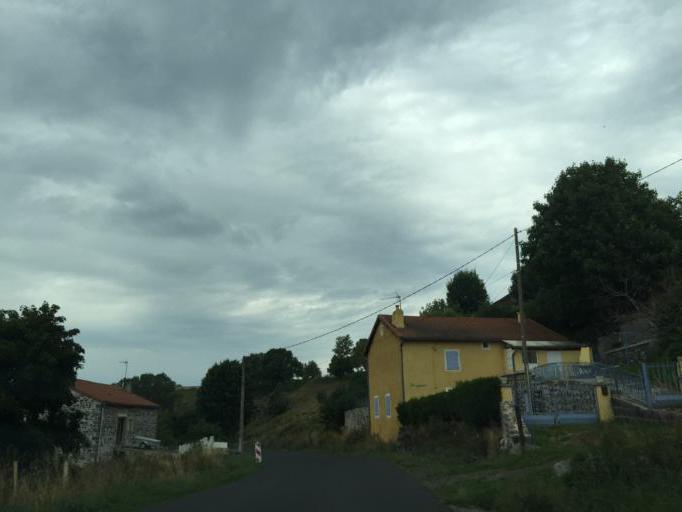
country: FR
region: Languedoc-Roussillon
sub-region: Departement de la Lozere
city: Langogne
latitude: 44.8359
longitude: 3.8109
